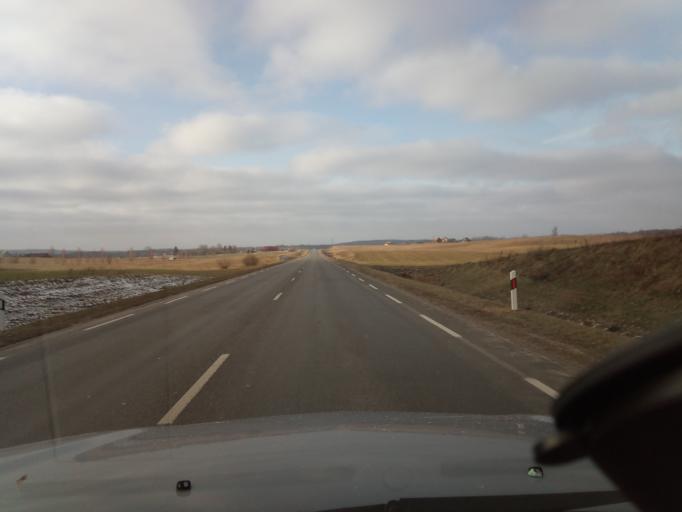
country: LT
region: Alytaus apskritis
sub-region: Alytus
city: Alytus
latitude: 54.3672
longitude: 24.1699
